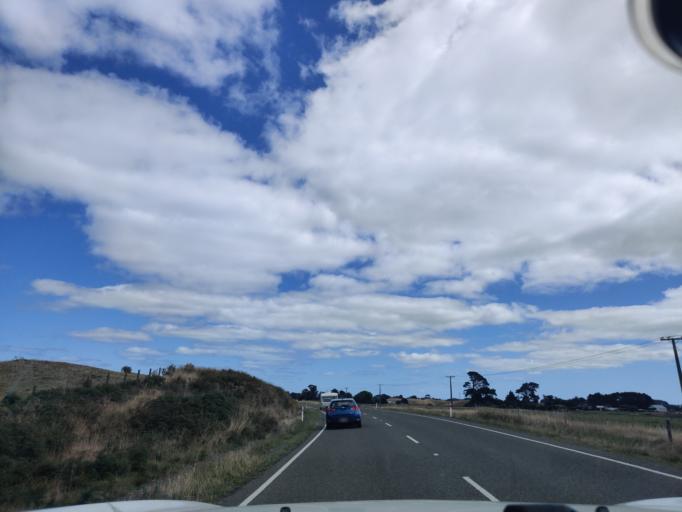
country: NZ
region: Manawatu-Wanganui
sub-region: Horowhenua District
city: Foxton
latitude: -40.4159
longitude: 175.4042
